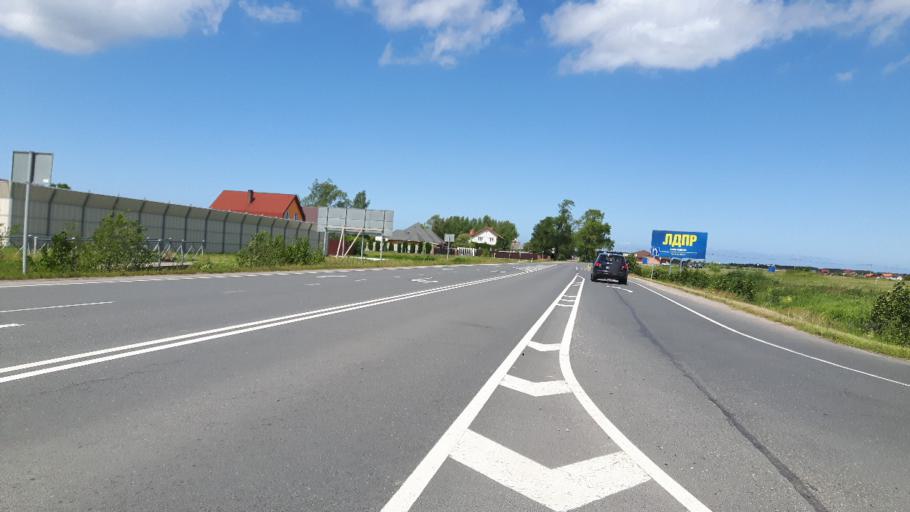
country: RU
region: Kaliningrad
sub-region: Zelenogradskiy Rayon
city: Zelenogradsk
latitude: 54.9241
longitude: 20.3982
